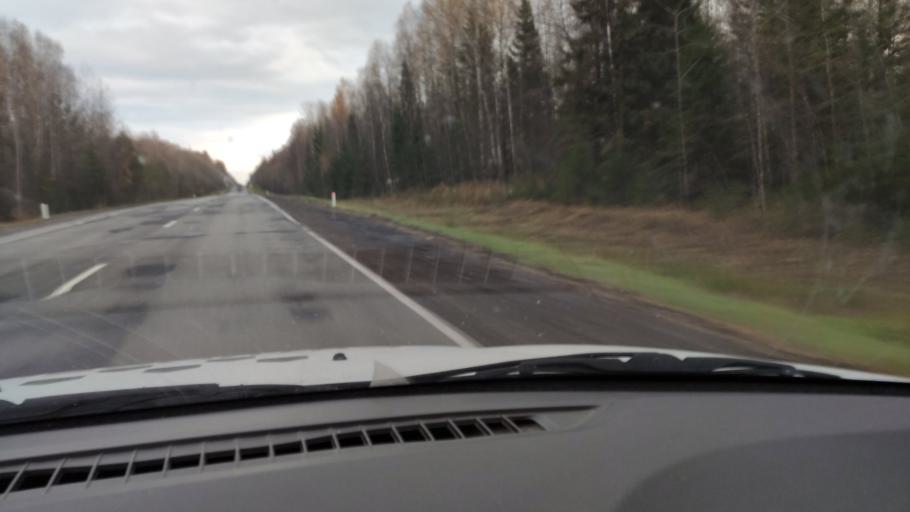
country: RU
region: Kirov
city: Omutninsk
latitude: 58.7661
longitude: 51.9805
